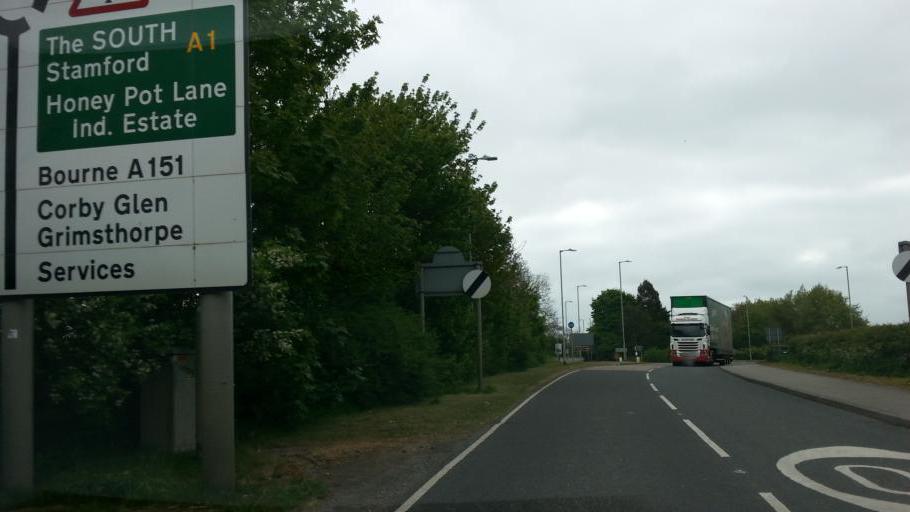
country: GB
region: England
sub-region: District of Rutland
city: Clipsham
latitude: 52.8032
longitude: -0.6146
